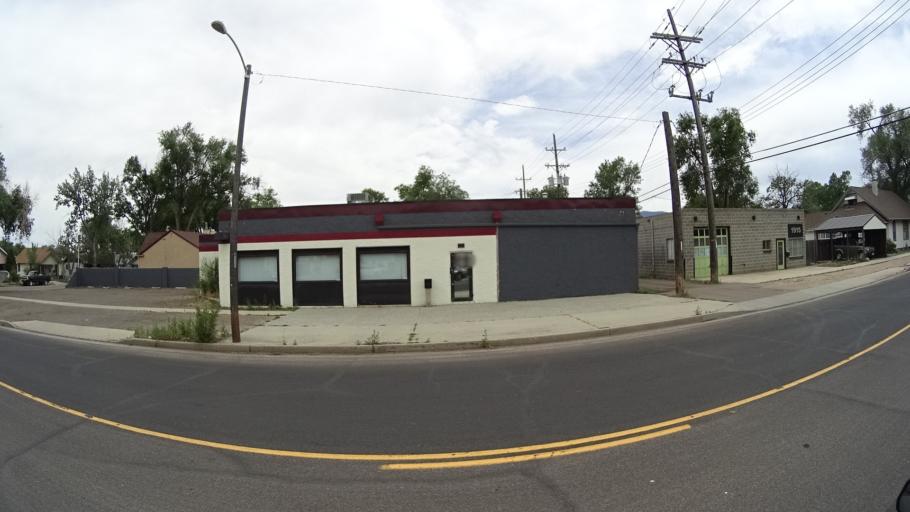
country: US
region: Colorado
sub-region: El Paso County
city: Colorado Springs
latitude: 38.8386
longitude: -104.7922
